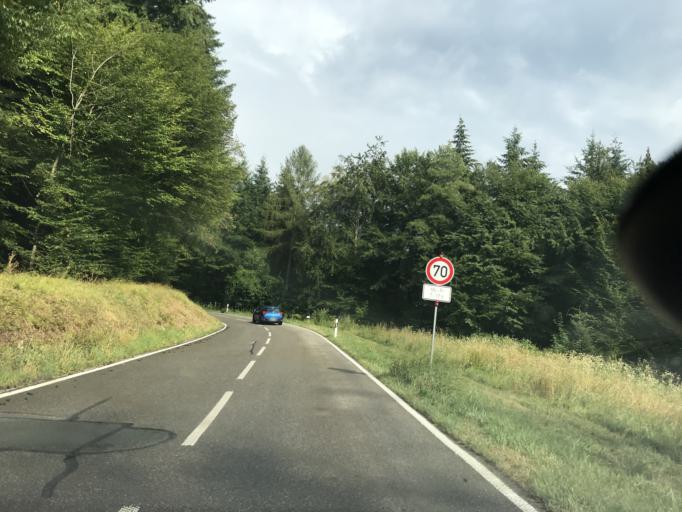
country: DE
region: Baden-Wuerttemberg
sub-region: Freiburg Region
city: Kandern
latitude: 47.7061
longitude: 7.6890
